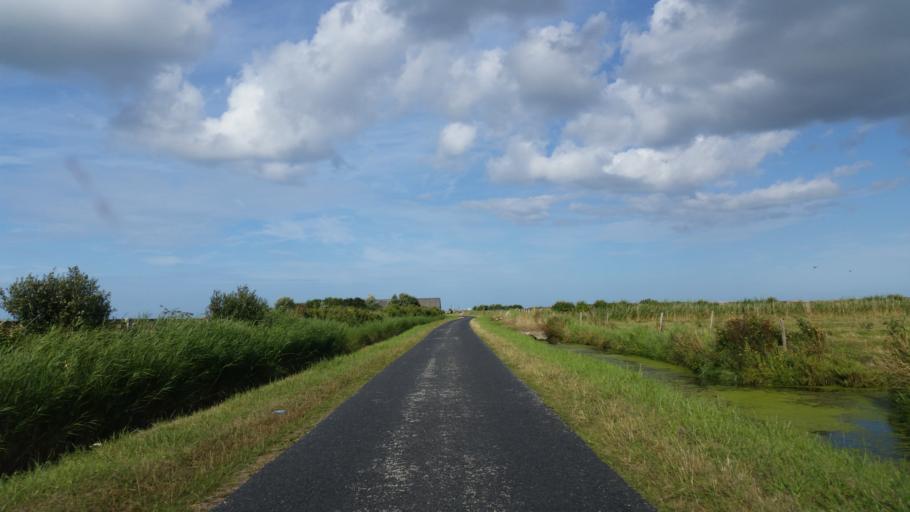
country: FR
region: Lower Normandy
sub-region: Departement de la Manche
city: Sainte-Mere-Eglise
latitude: 49.4565
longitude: -1.2337
